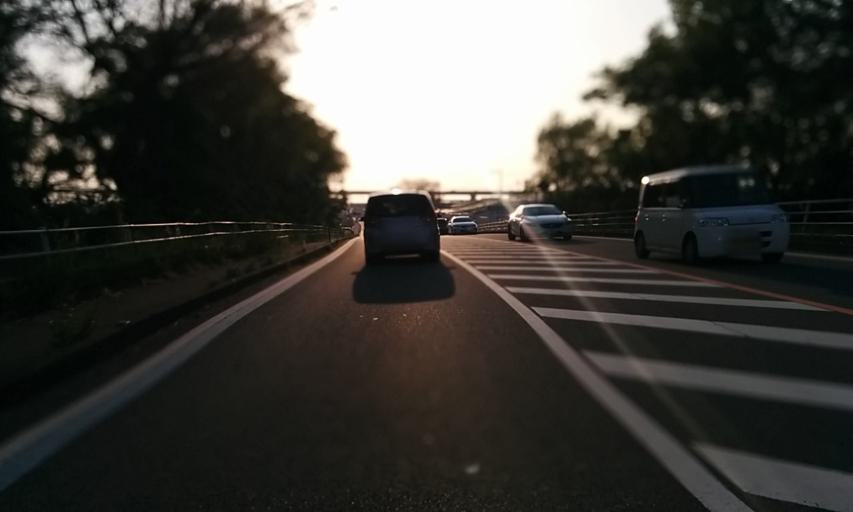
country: JP
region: Ehime
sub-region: Shikoku-chuo Shi
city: Matsuyama
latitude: 33.7891
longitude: 132.7786
